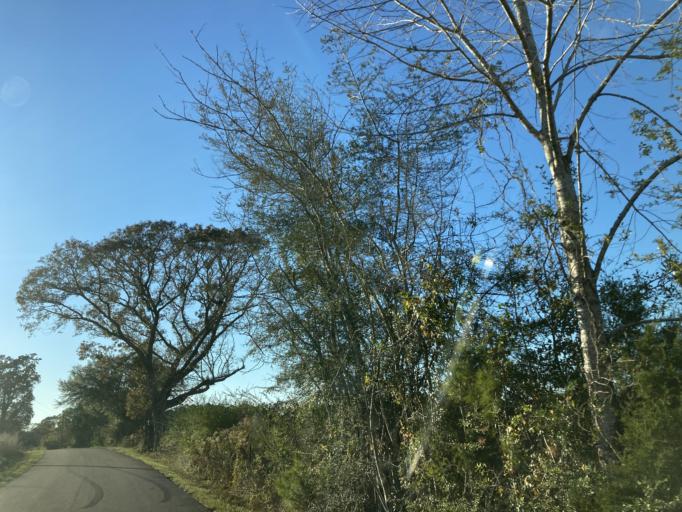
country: US
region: Mississippi
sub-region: Lamar County
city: Sumrall
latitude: 31.2680
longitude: -89.5998
